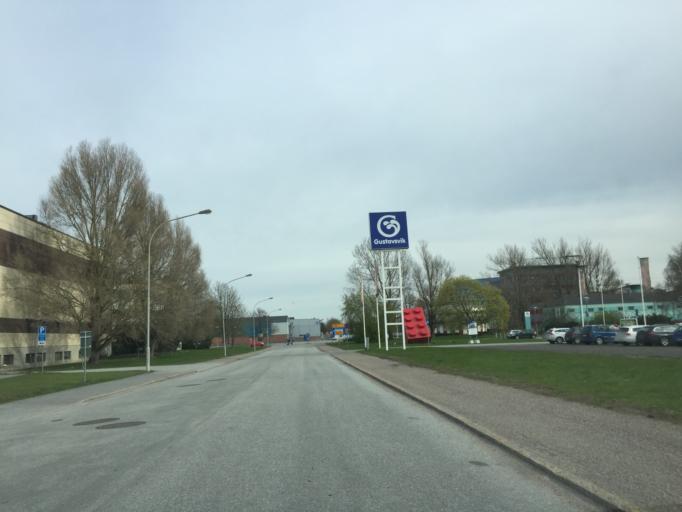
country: SE
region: OErebro
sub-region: Orebro Kommun
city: Orebro
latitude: 59.2614
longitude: 15.1951
